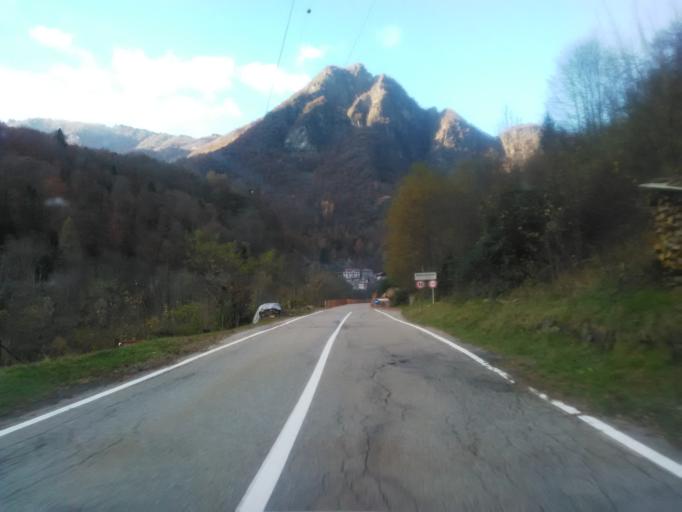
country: IT
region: Piedmont
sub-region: Provincia di Vercelli
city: Cravagliana
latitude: 45.8511
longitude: 8.1876
